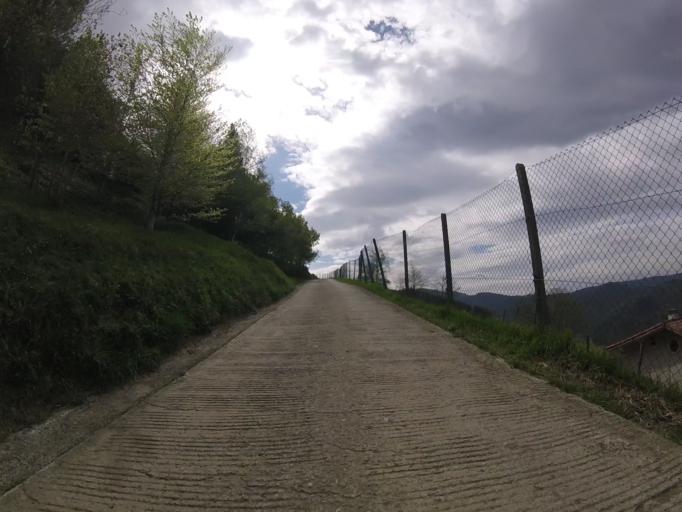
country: ES
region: Basque Country
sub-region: Provincia de Guipuzcoa
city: Aizarnazabal
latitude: 43.2470
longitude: -2.1944
